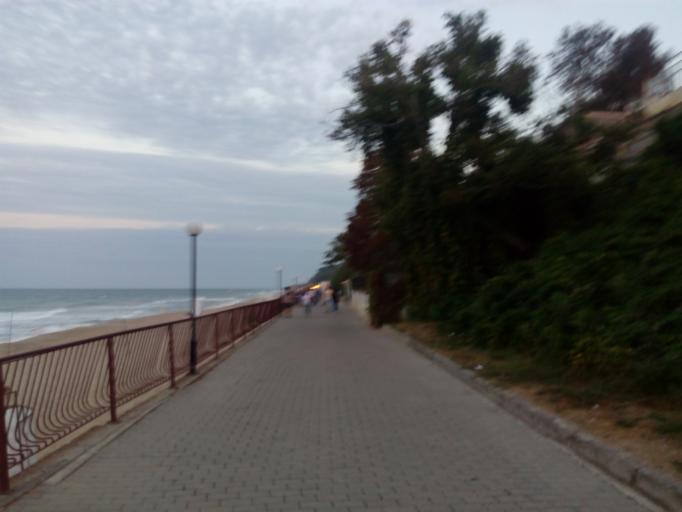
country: BG
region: Burgas
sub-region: Obshtina Nesebur
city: Obzor
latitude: 42.8176
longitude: 27.8852
